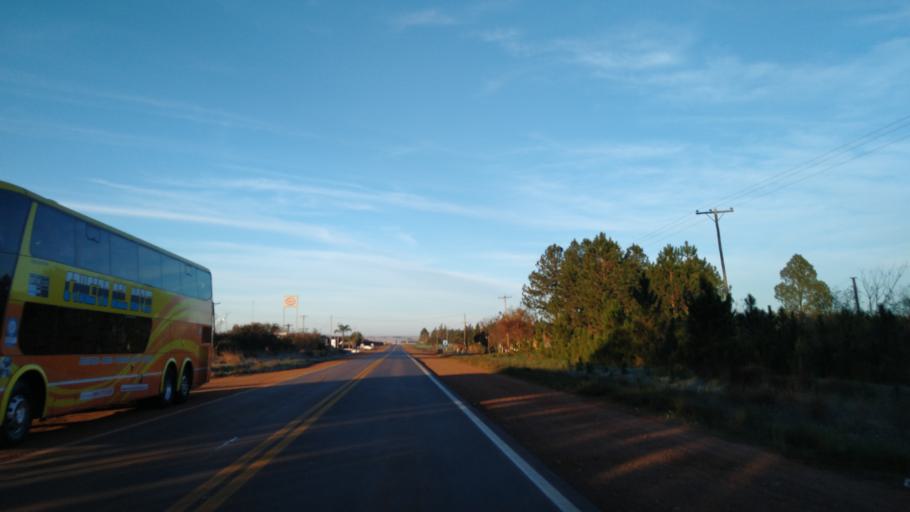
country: AR
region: Corrientes
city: Santo Tome
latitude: -28.5783
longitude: -56.0850
